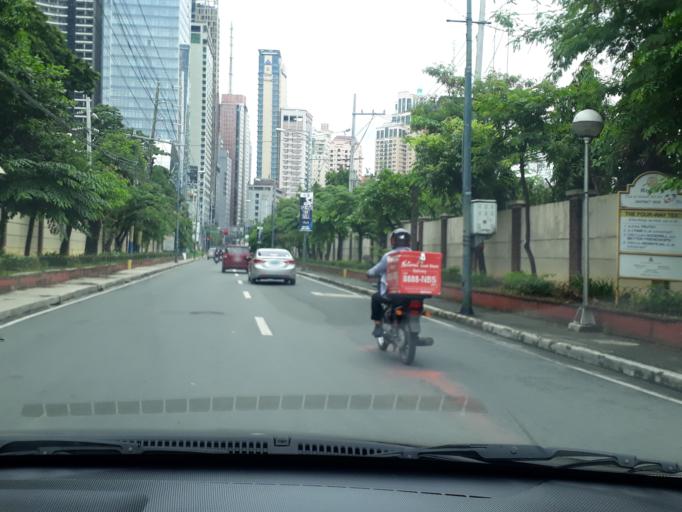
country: PH
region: Metro Manila
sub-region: Makati City
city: Makati City
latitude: 14.5660
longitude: 121.0254
